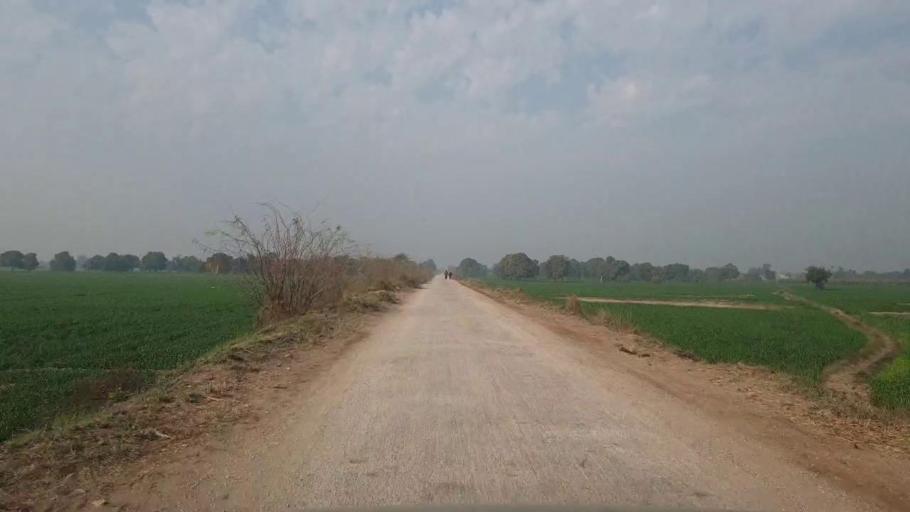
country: PK
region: Sindh
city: Hala
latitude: 25.9074
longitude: 68.4375
